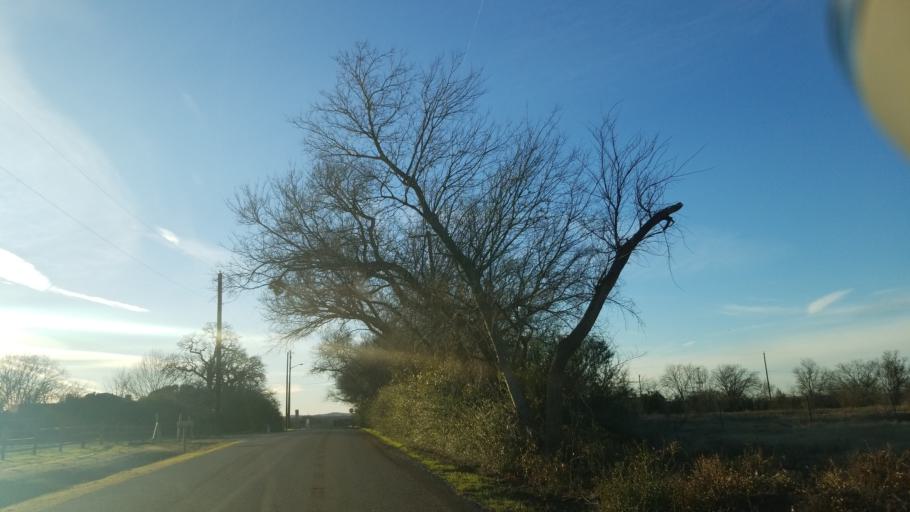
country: US
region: Texas
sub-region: Denton County
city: Denton
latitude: 33.1839
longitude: -97.1616
